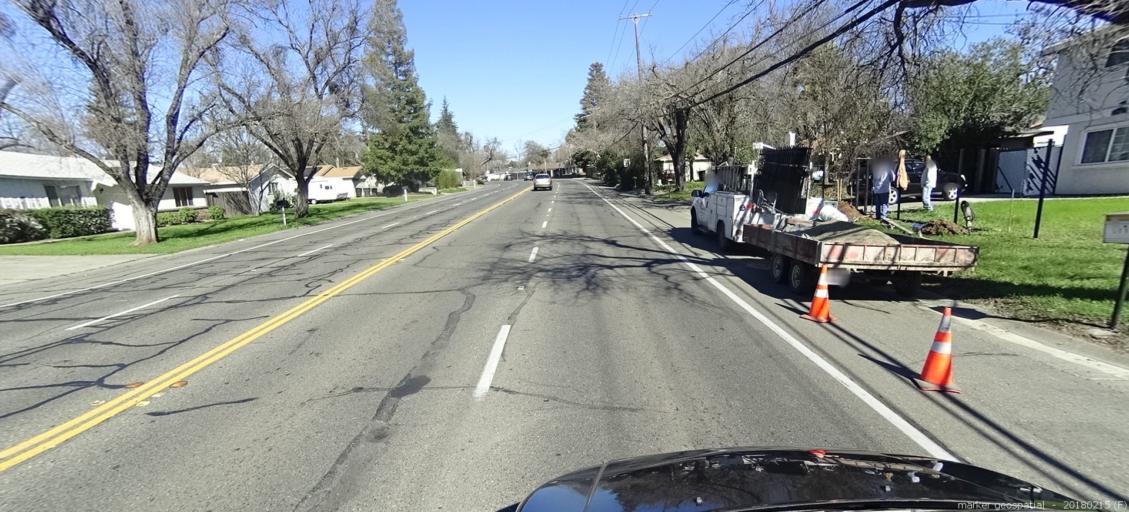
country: US
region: California
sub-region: Sacramento County
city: Foothill Farms
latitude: 38.6698
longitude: -121.3086
